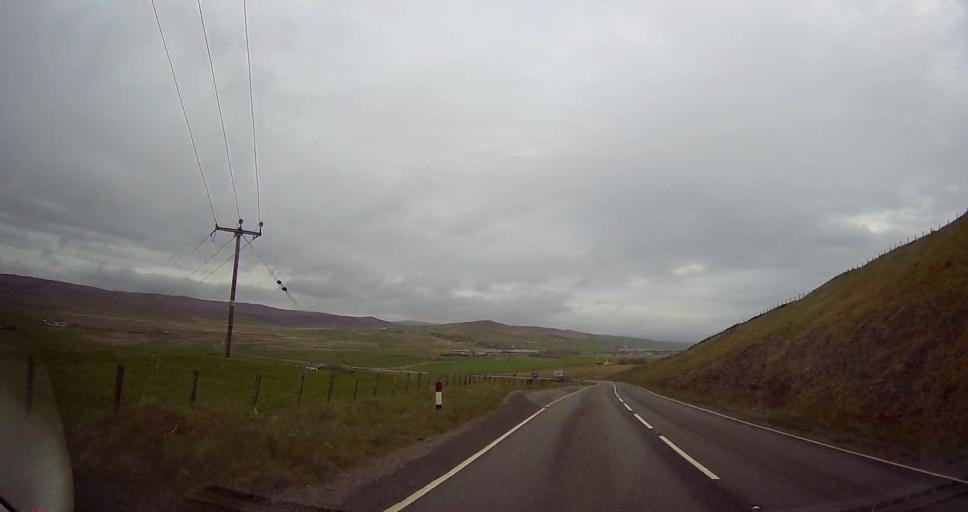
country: GB
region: Scotland
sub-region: Shetland Islands
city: Lerwick
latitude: 60.1817
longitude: -1.2250
